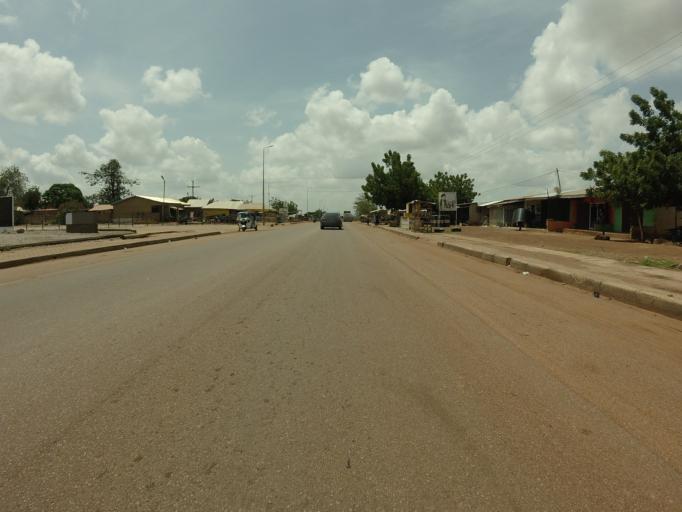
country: GH
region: Northern
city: Tamale
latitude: 9.3777
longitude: -0.8693
